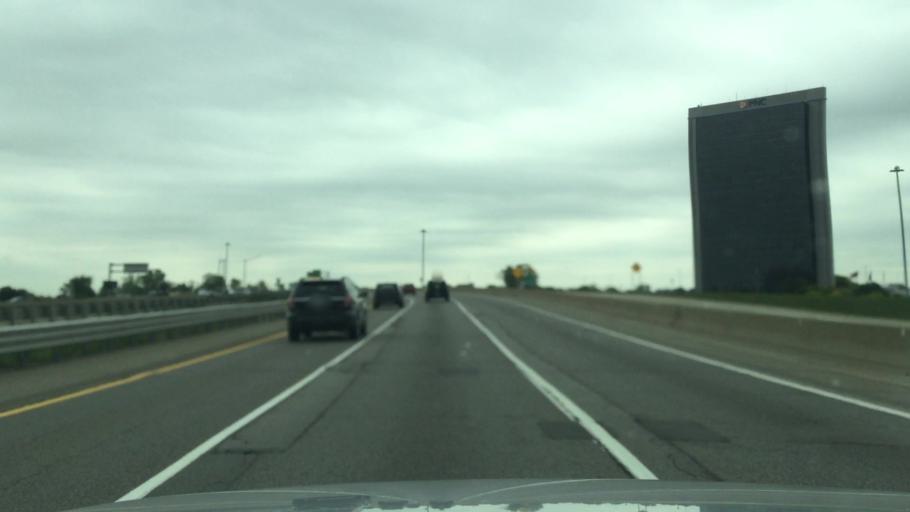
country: US
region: Michigan
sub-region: Oakland County
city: Clawson
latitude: 42.5646
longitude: -83.1590
